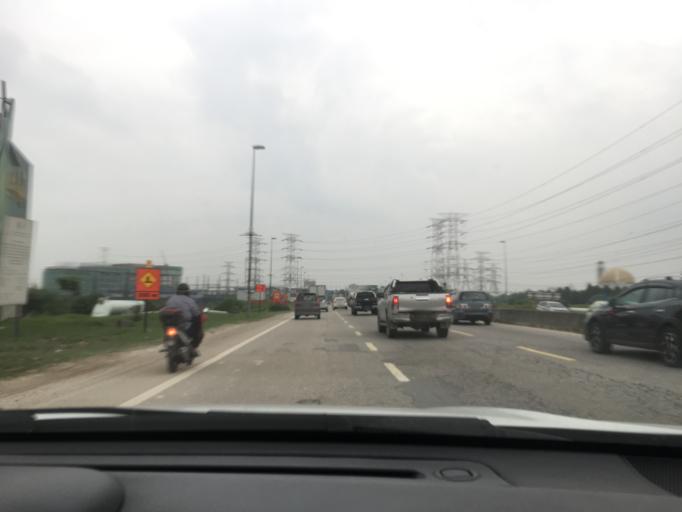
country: MY
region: Selangor
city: Klang
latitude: 3.1007
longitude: 101.4425
